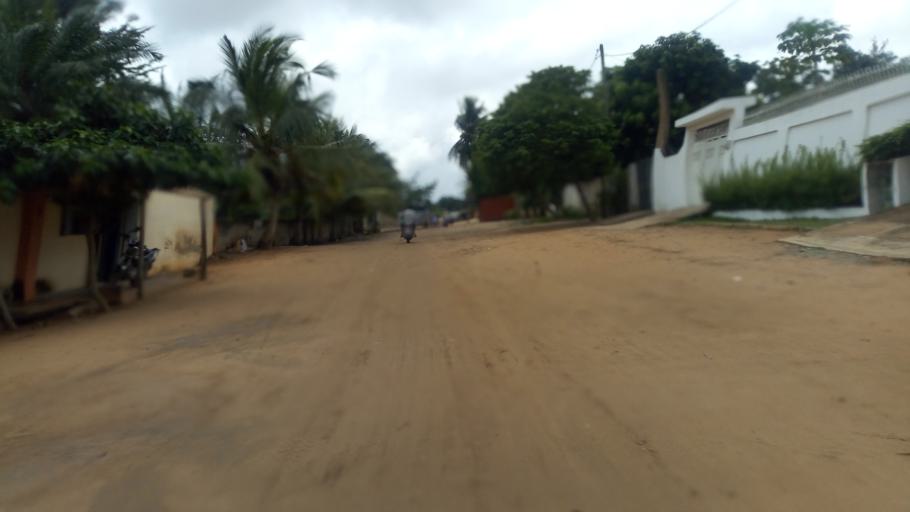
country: TG
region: Maritime
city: Lome
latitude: 6.1822
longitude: 1.1674
